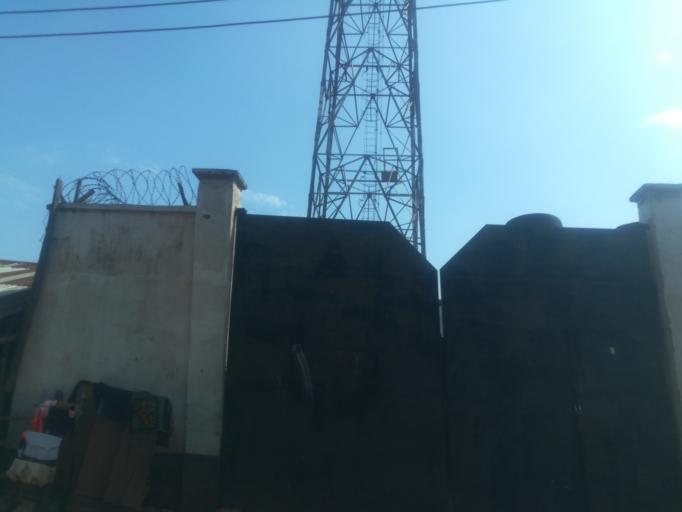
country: NG
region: Oyo
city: Ibadan
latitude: 7.4178
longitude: 3.9768
